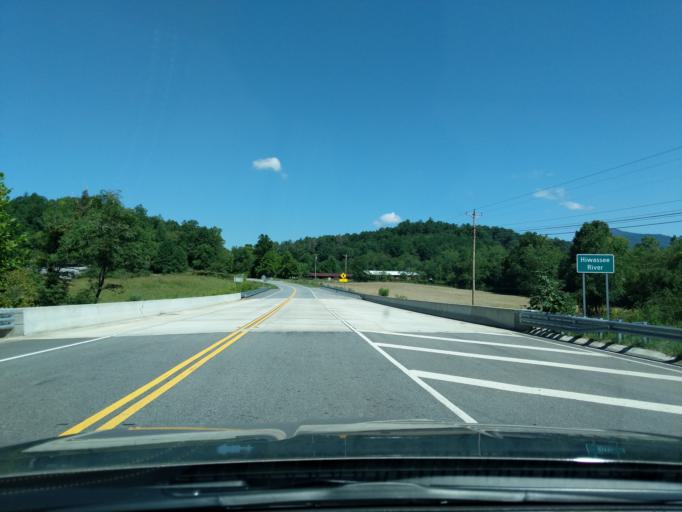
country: US
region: Georgia
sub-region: Towns County
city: Hiawassee
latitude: 34.9028
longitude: -83.7223
